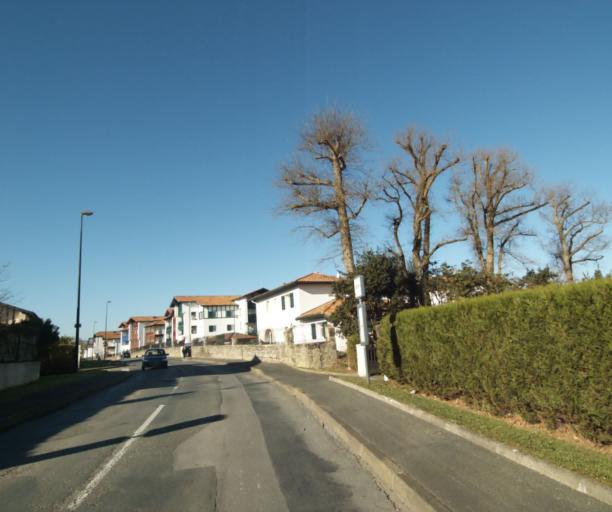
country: FR
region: Aquitaine
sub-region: Departement des Pyrenees-Atlantiques
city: Ciboure
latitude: 43.3761
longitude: -1.6708
